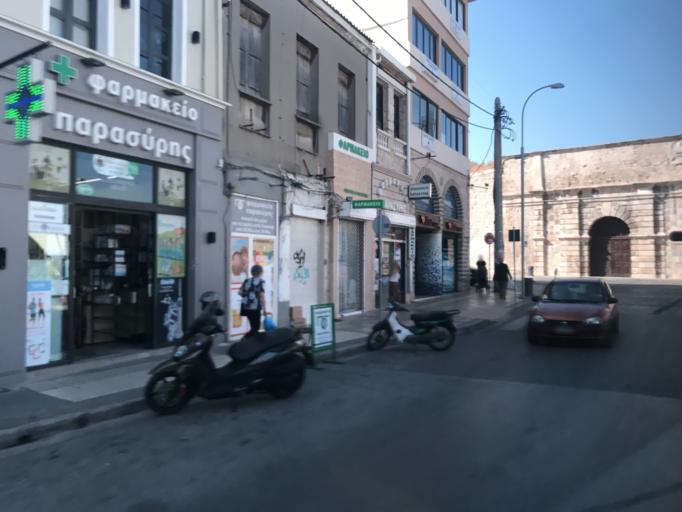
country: GR
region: Crete
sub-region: Nomos Irakleiou
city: Irakleion
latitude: 35.3375
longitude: 25.1256
